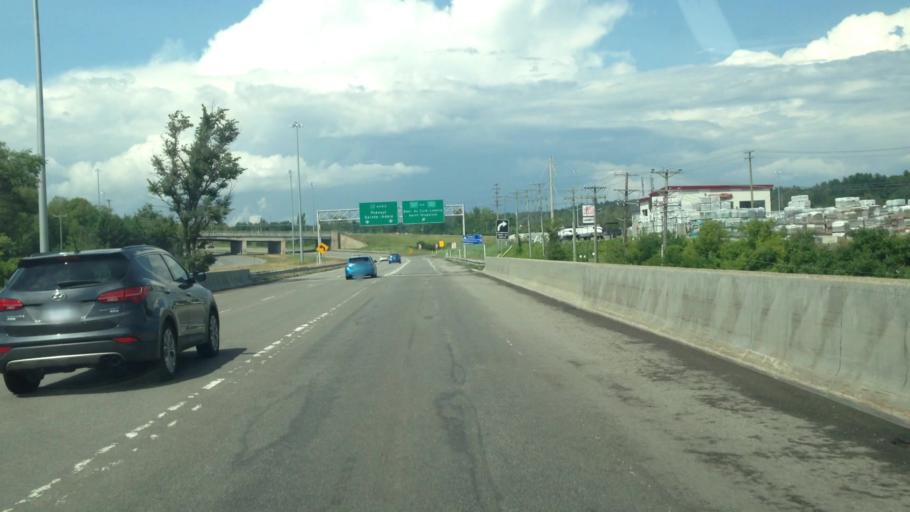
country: CA
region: Quebec
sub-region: Laurentides
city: Saint-Jerome
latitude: 45.8038
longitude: -74.0187
